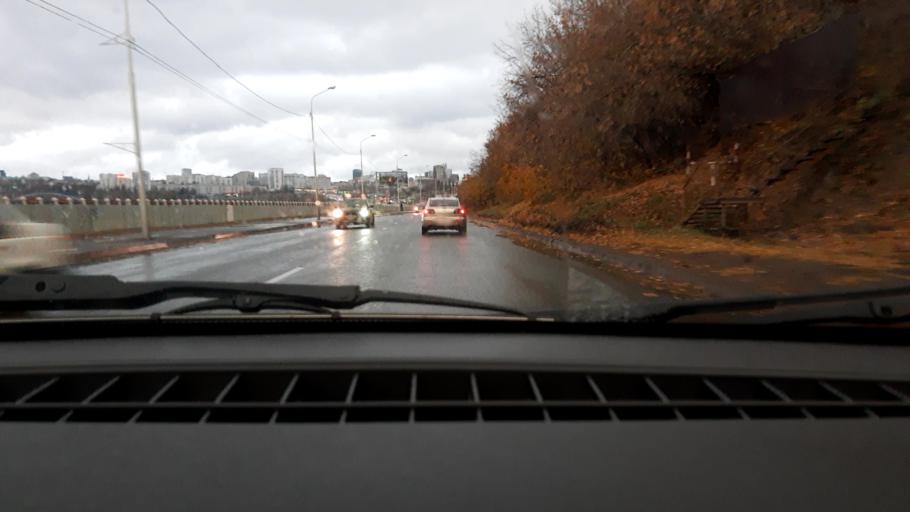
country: RU
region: Bashkortostan
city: Ufa
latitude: 54.7025
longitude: 55.9681
